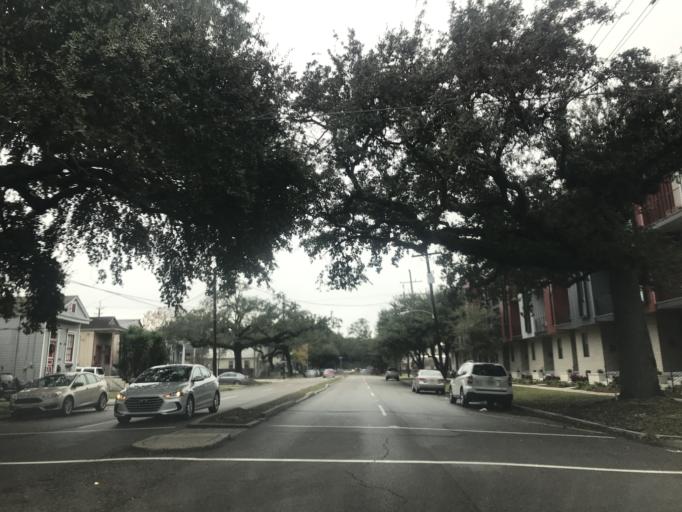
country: US
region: Louisiana
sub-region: Orleans Parish
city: New Orleans
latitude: 29.9736
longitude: -90.0952
